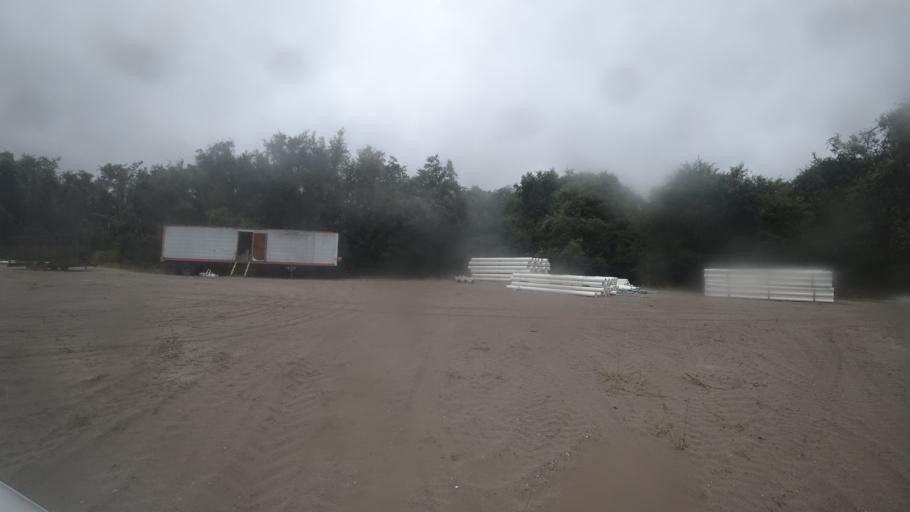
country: US
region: Florida
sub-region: Hillsborough County
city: Wimauma
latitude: 27.5661
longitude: -82.3123
